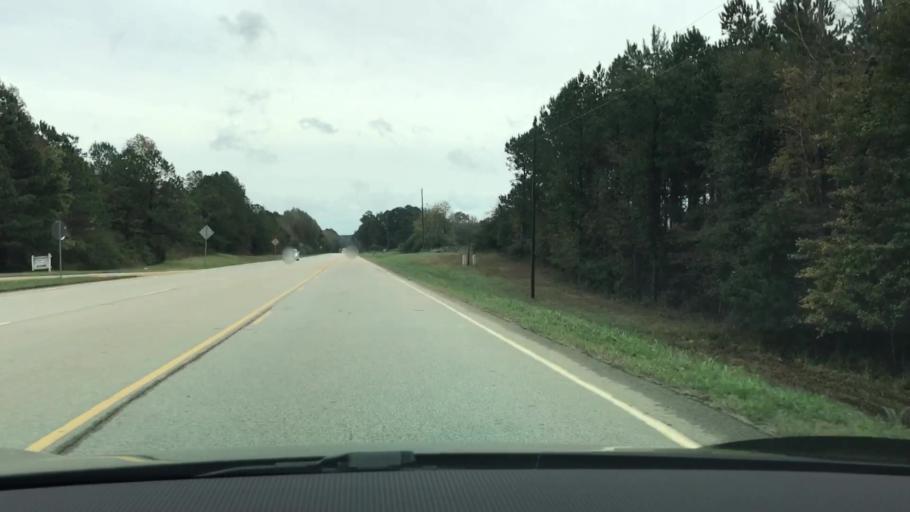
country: US
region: Georgia
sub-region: Warren County
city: Firing Range
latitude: 33.4799
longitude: -82.7541
